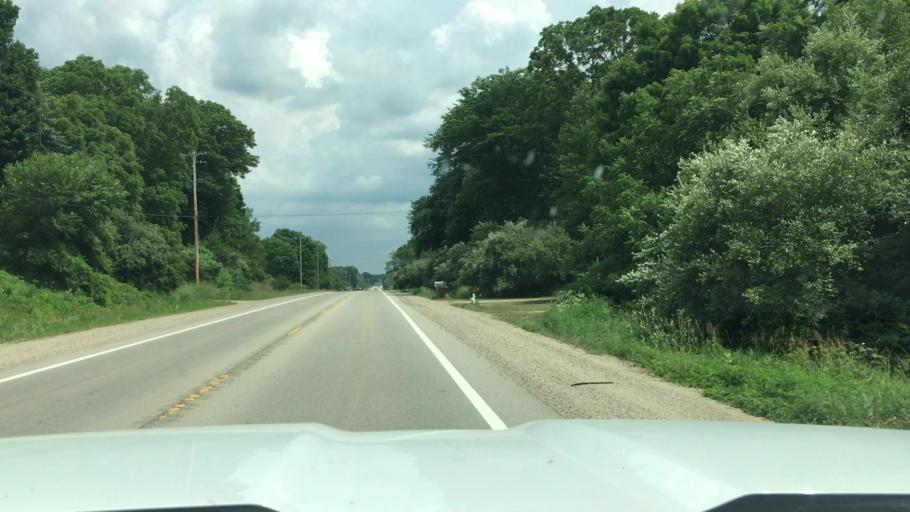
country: US
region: Michigan
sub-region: Montcalm County
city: Greenville
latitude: 43.1764
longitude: -85.3984
